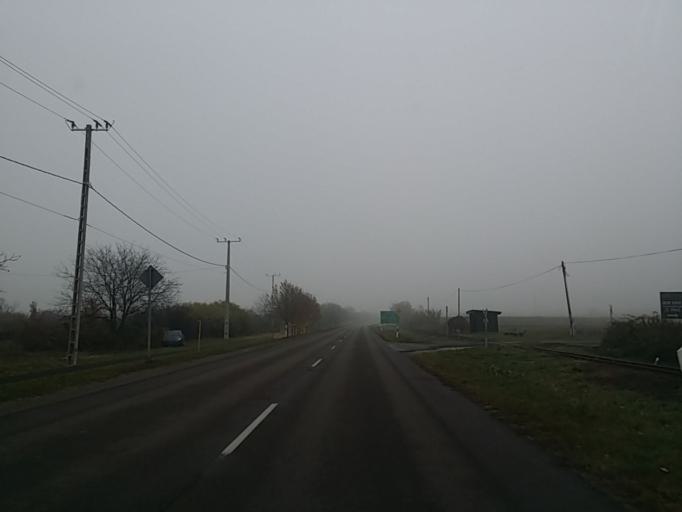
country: HU
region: Heves
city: Gyongyossolymos
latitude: 47.8055
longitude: 19.9504
